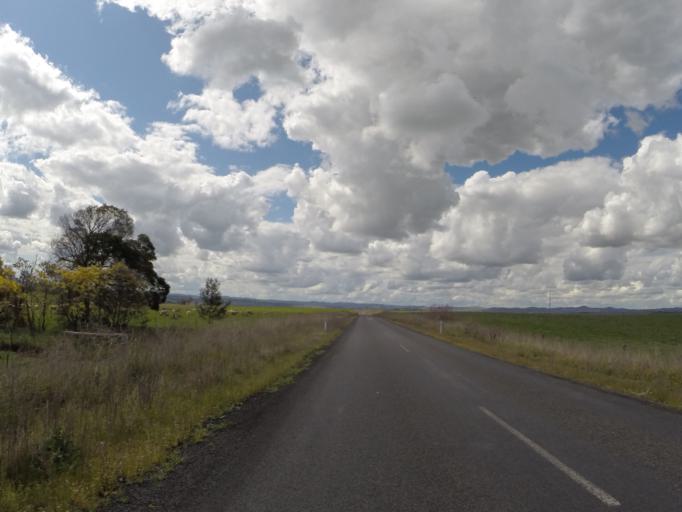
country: AU
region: New South Wales
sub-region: Yass Valley
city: Yass
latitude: -34.9050
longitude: 148.8884
